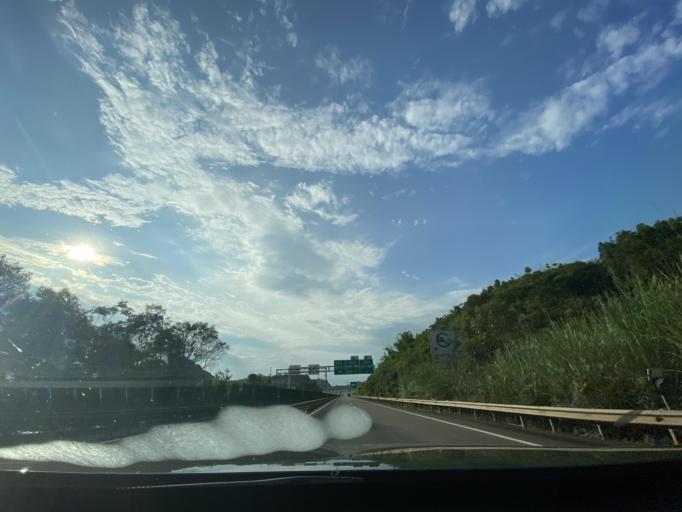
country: CN
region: Sichuan
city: Jiancheng
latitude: 30.3570
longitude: 104.5294
